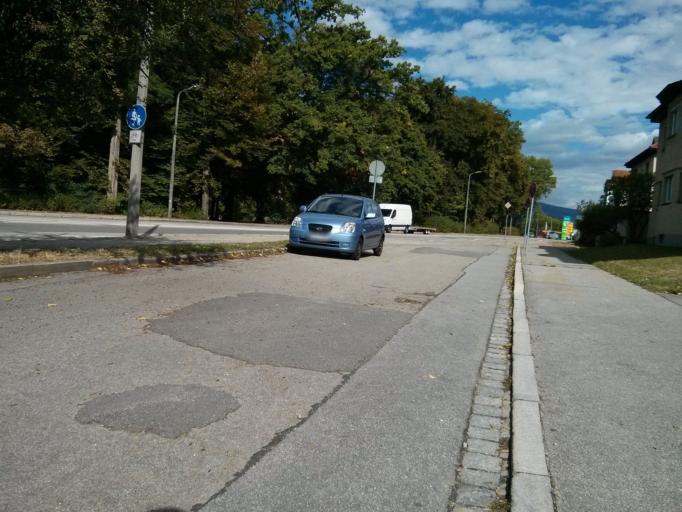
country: DE
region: Bavaria
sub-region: Lower Bavaria
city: Deggendorf
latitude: 48.8424
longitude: 12.9599
